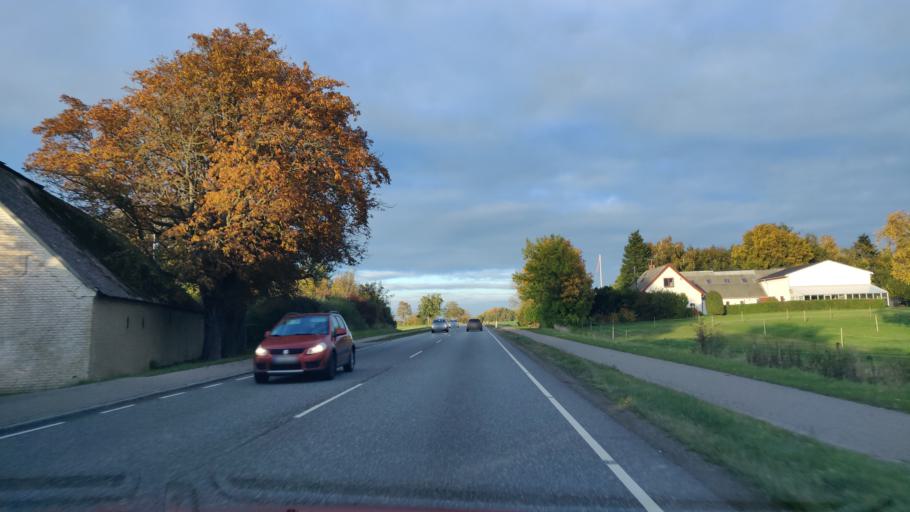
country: DK
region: Zealand
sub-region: Holbaek Kommune
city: Vipperod
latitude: 55.6621
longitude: 11.6815
